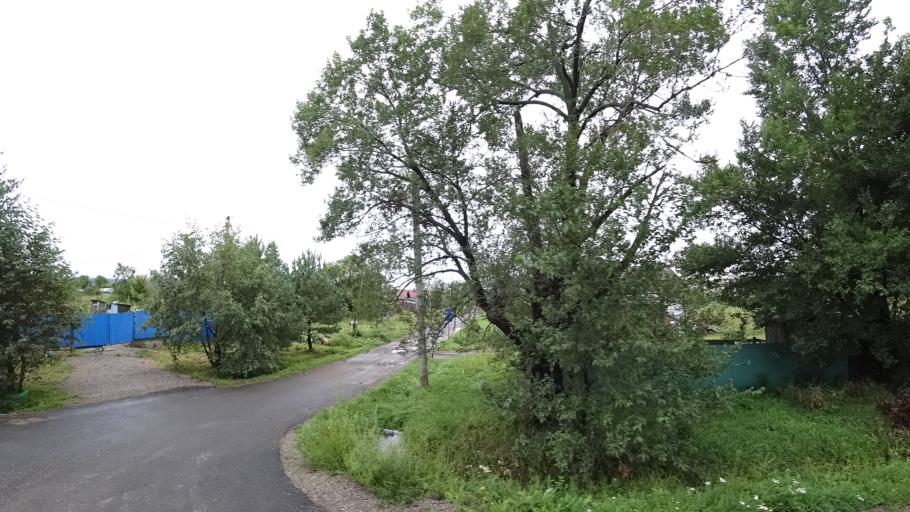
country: RU
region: Primorskiy
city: Monastyrishche
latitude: 44.1990
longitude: 132.4966
